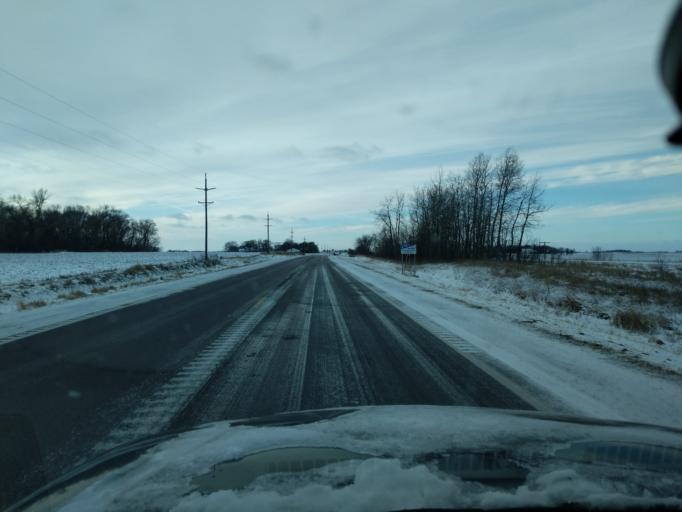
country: US
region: Minnesota
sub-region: Renville County
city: Hector
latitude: 44.7243
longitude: -94.5298
